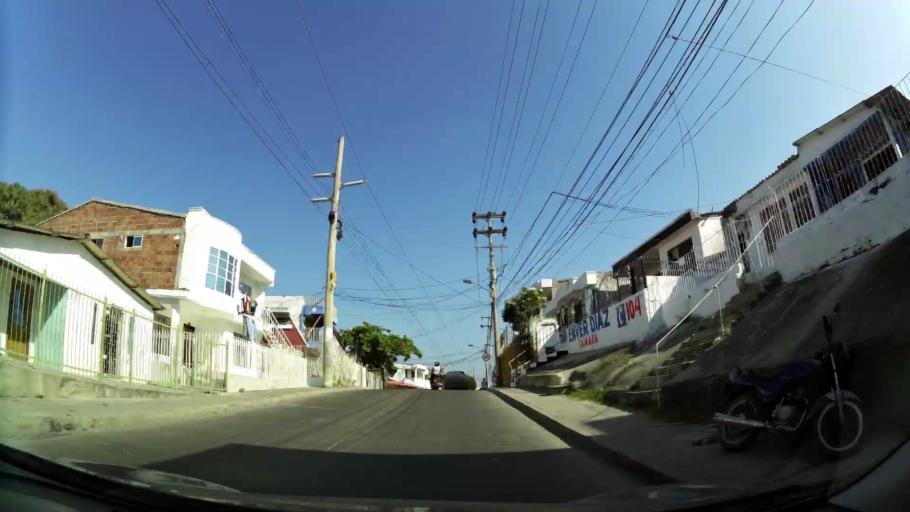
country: CO
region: Bolivar
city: Cartagena
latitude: 10.3978
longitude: -75.4970
